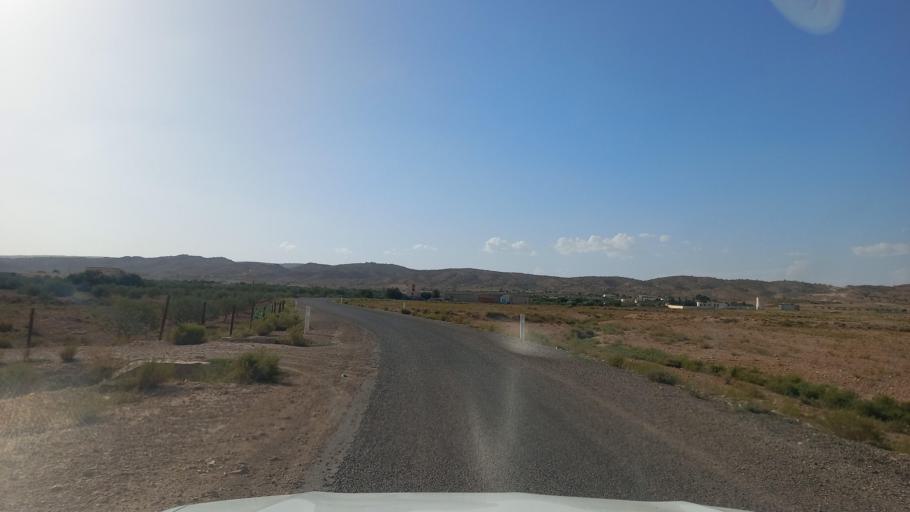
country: TN
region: Al Qasrayn
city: Sbiba
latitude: 35.3406
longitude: 8.9941
